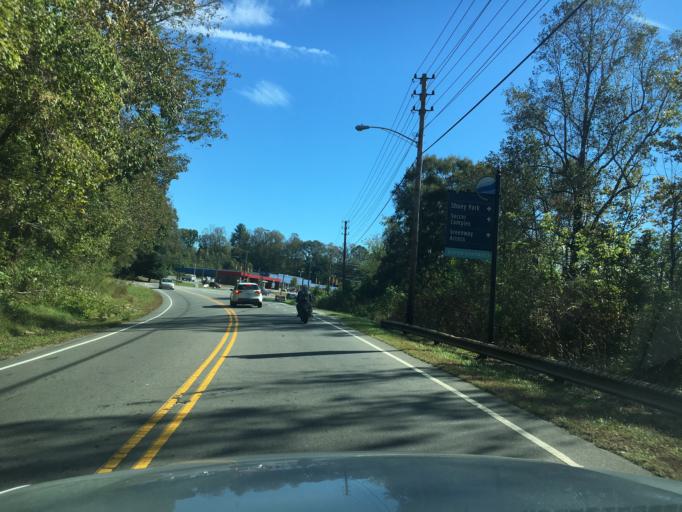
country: US
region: North Carolina
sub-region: Burke County
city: Morganton
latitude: 35.7510
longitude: -81.7055
